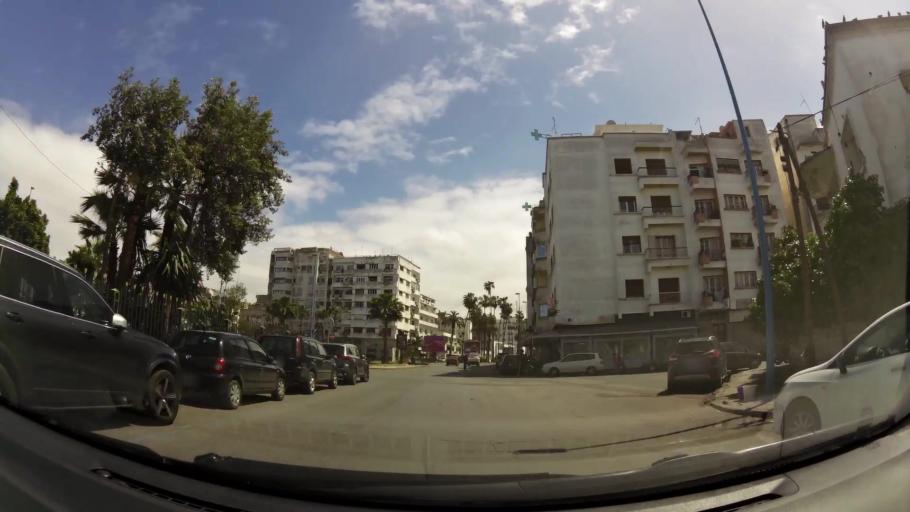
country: MA
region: Grand Casablanca
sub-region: Casablanca
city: Casablanca
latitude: 33.5987
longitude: -7.6328
